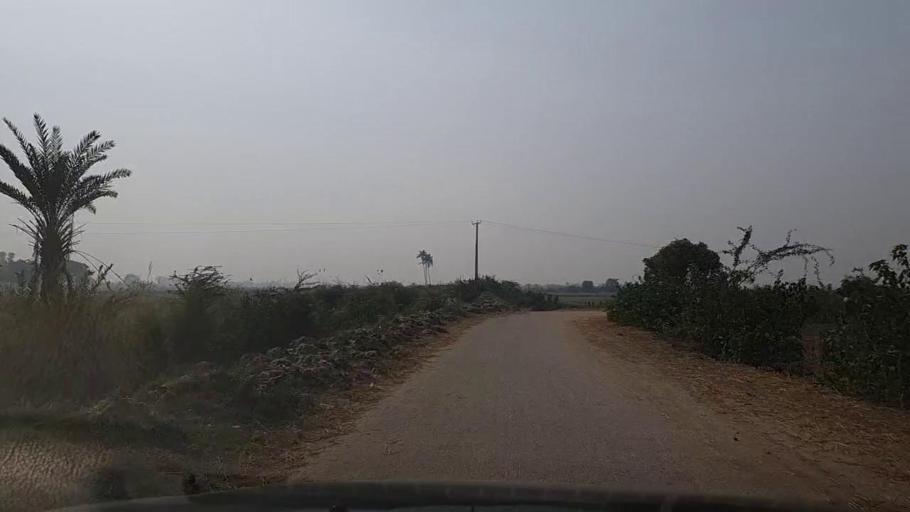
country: PK
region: Sindh
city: Mirpur Sakro
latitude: 24.5477
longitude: 67.8340
